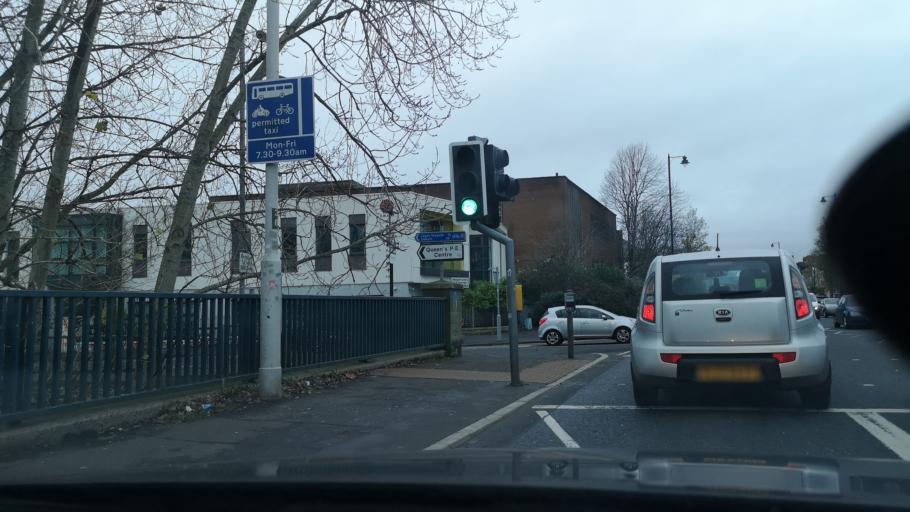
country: GB
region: Northern Ireland
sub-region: City of Belfast
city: Belfast
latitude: 54.5831
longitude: -5.9222
